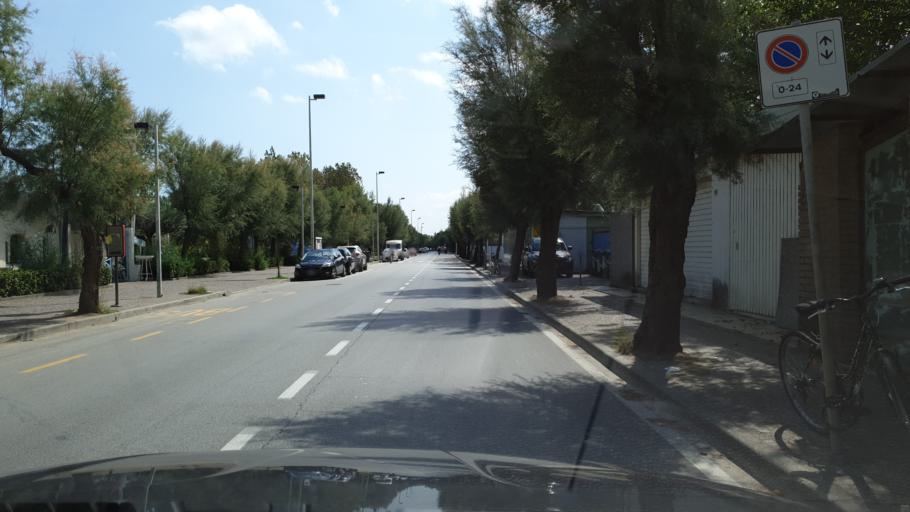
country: IT
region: Emilia-Romagna
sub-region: Provincia di Rimini
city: Riccione
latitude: 43.9929
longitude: 12.6760
